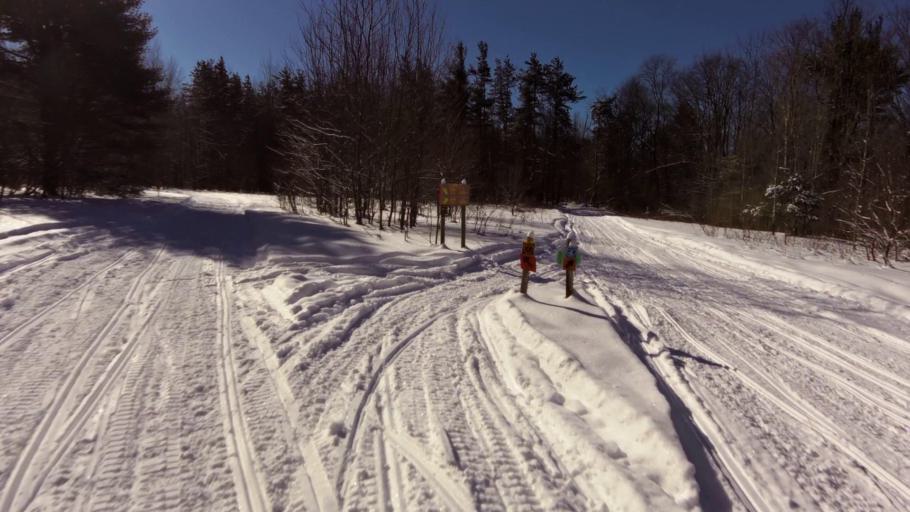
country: US
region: New York
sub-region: Chautauqua County
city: Fredonia
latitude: 42.3507
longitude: -79.1875
